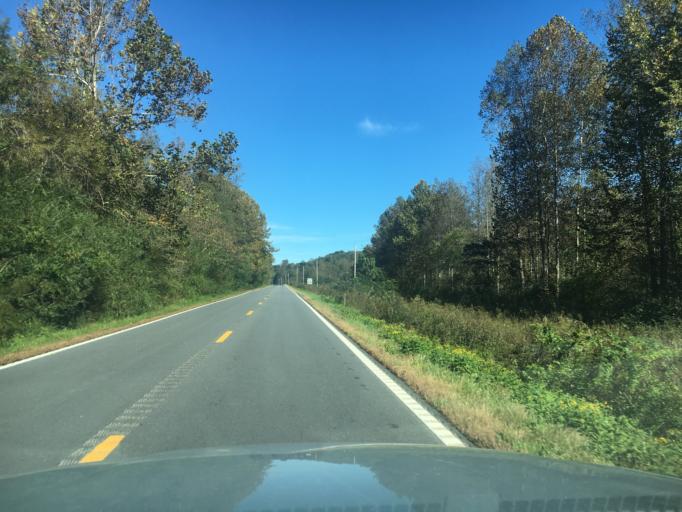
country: US
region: North Carolina
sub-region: Rutherford County
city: Spindale
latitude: 35.5450
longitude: -81.8561
